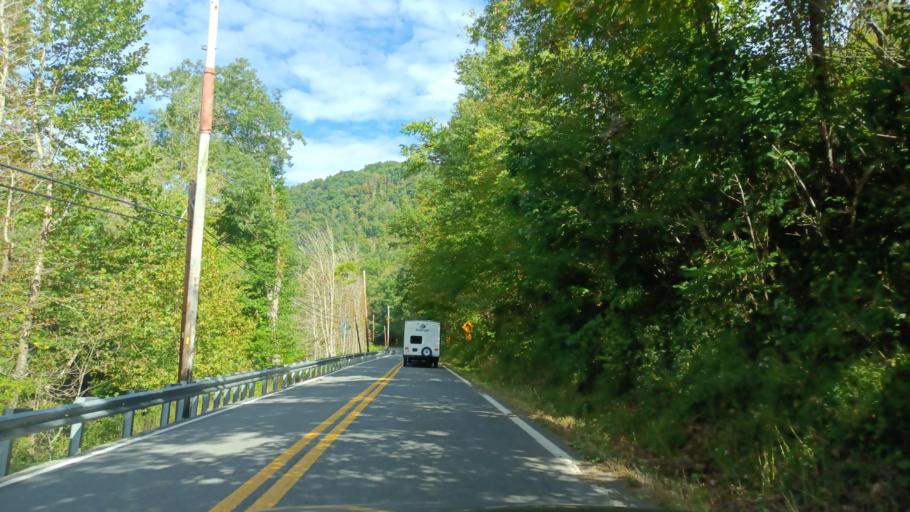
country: US
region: West Virginia
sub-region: Preston County
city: Terra Alta
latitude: 39.3027
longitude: -79.6359
